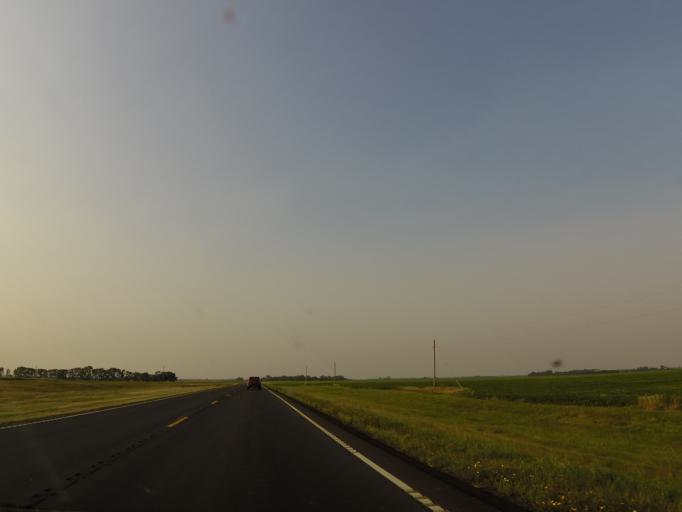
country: US
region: North Dakota
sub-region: Traill County
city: Mayville
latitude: 47.4521
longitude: -97.3260
